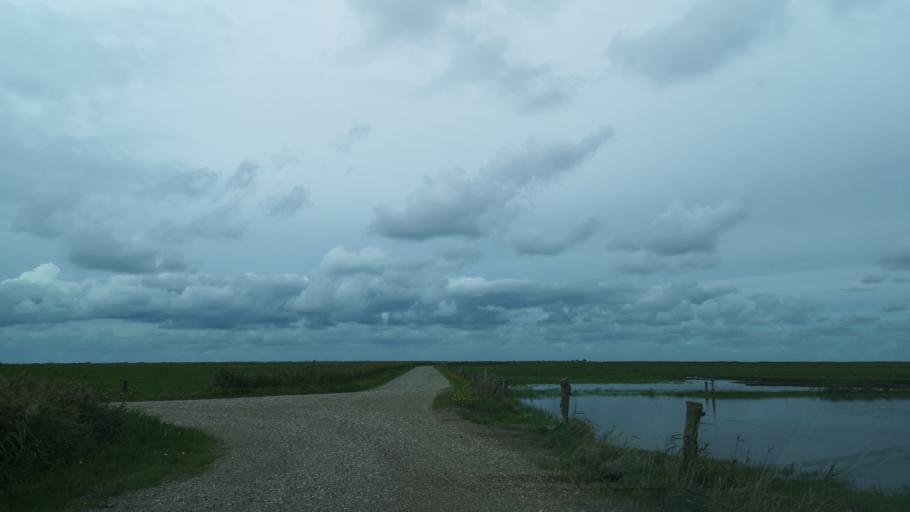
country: DK
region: Central Jutland
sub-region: Ringkobing-Skjern Kommune
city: Hvide Sande
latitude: 55.8684
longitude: 8.2300
